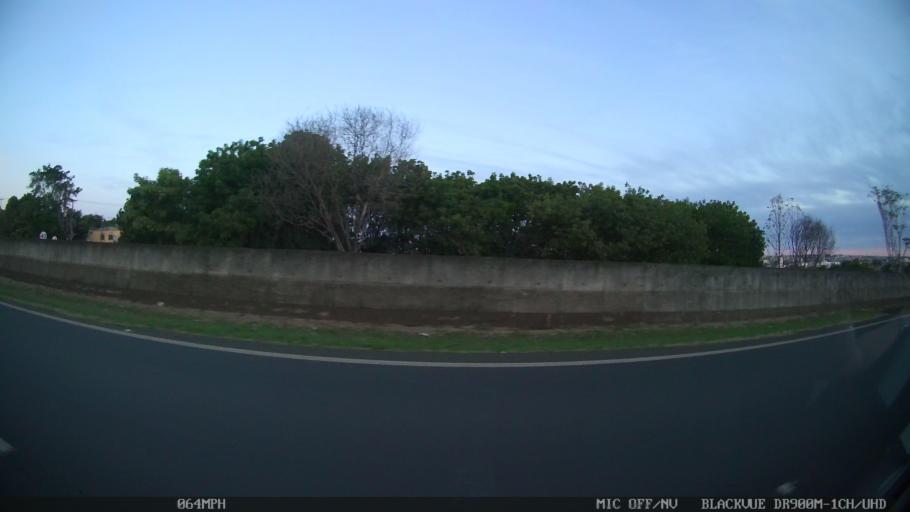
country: BR
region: Sao Paulo
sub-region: Catanduva
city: Catanduva
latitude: -21.1129
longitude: -48.9720
